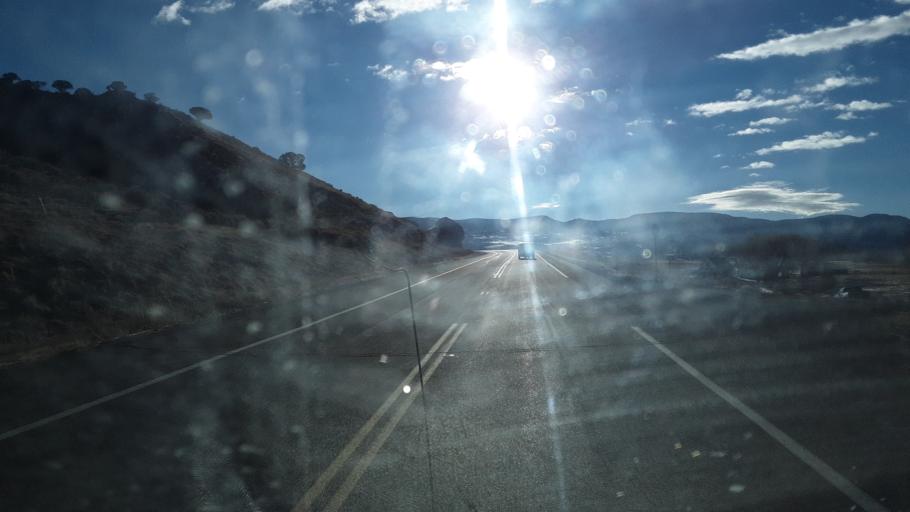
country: US
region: Colorado
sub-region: Montrose County
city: Montrose
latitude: 38.4056
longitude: -107.5139
